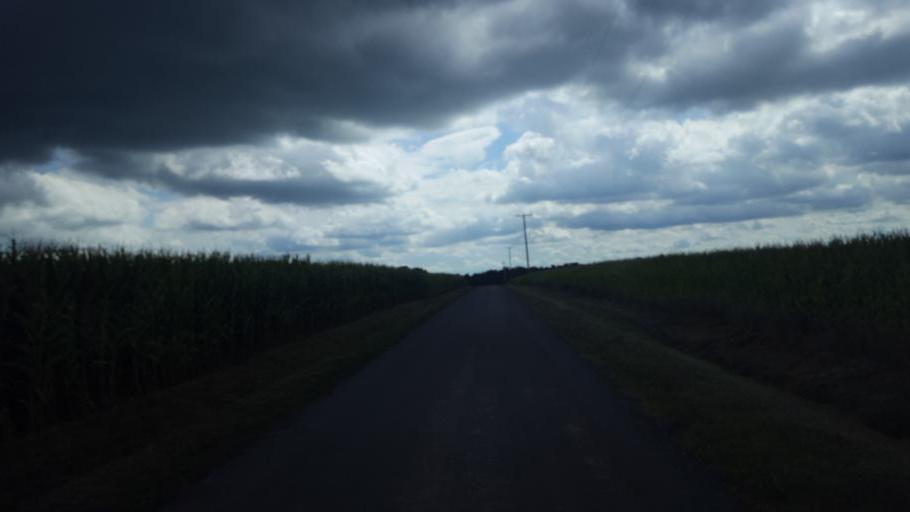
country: US
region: Ohio
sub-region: Huron County
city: Greenwich
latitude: 40.9633
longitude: -82.5299
